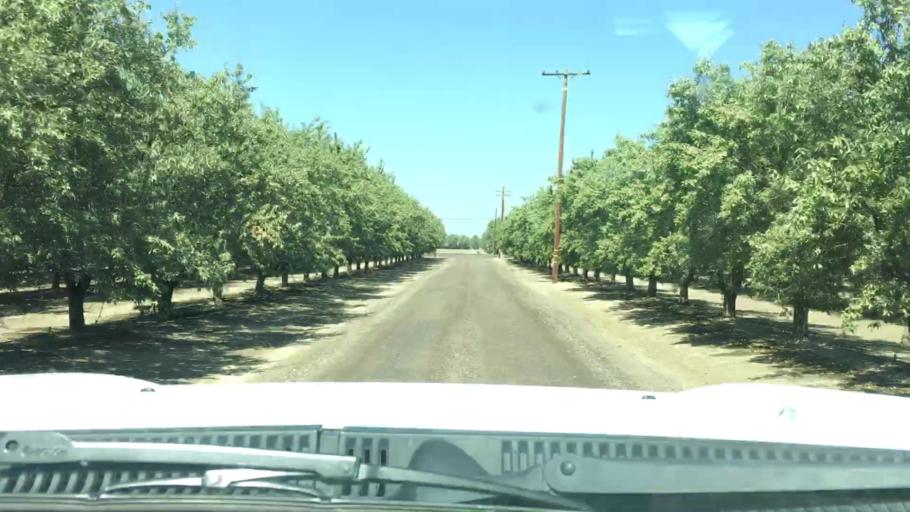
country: US
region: California
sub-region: Kern County
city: Shafter
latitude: 35.4986
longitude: -119.3273
